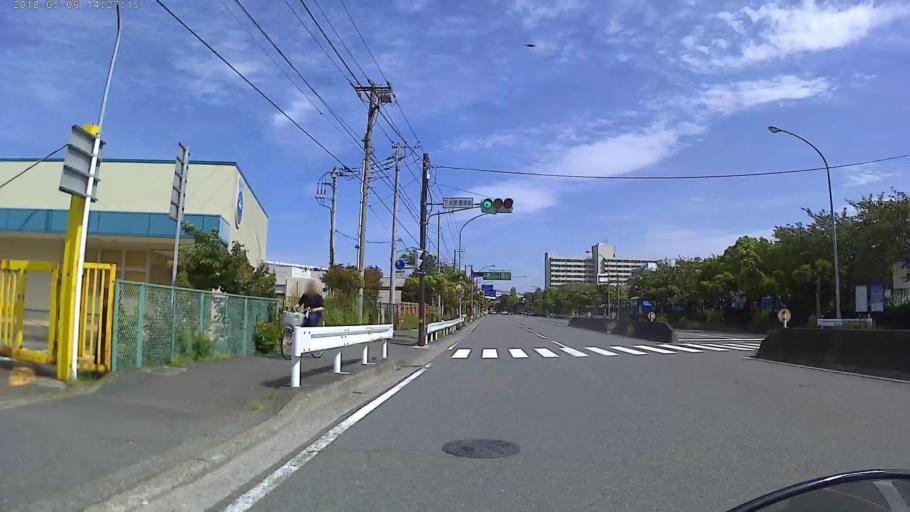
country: JP
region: Kanagawa
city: Yokohama
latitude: 35.4335
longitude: 139.6672
